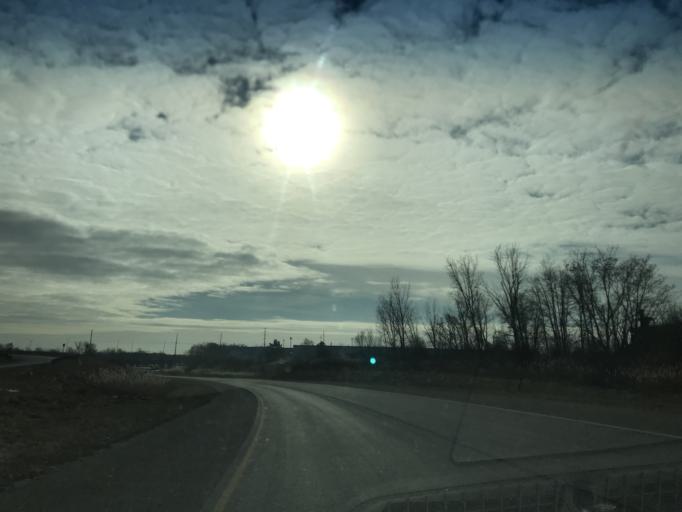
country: US
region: Michigan
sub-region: Oakland County
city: Auburn Hills
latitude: 42.6535
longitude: -83.2404
